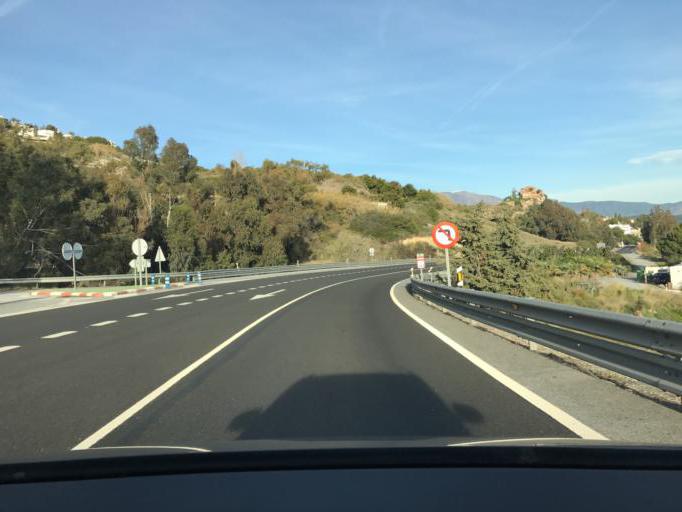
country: ES
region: Andalusia
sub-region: Provincia de Granada
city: Salobrena
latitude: 36.7452
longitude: -3.6140
